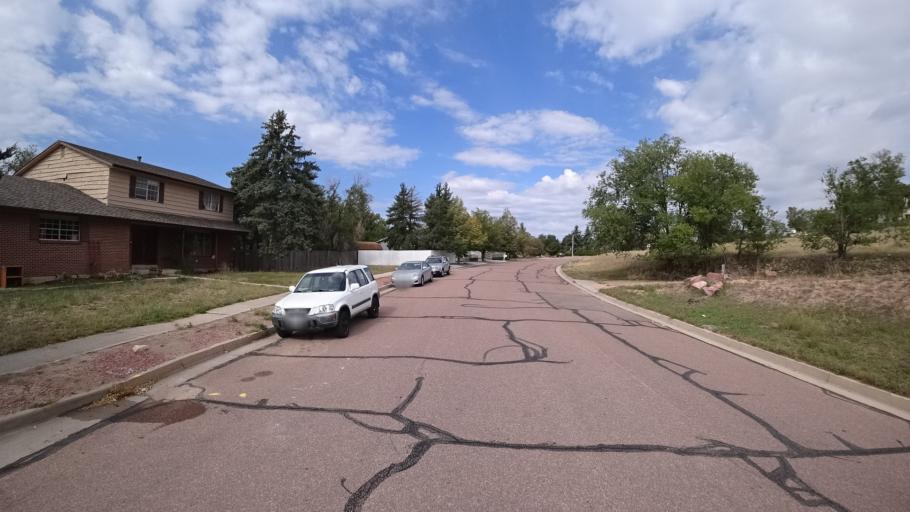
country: US
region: Colorado
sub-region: El Paso County
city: Cimarron Hills
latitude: 38.8502
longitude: -104.7261
